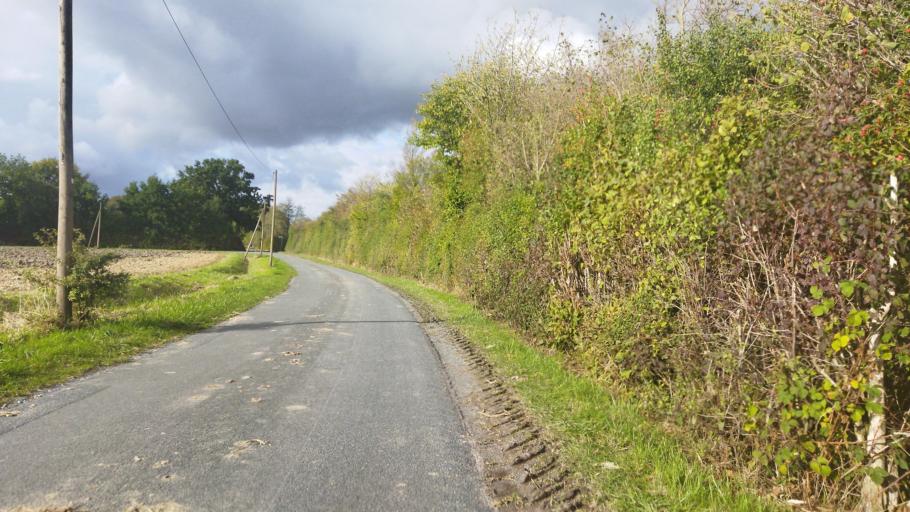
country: DE
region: North Rhine-Westphalia
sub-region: Regierungsbezirk Munster
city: Billerbeck
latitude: 51.9088
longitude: 7.2609
